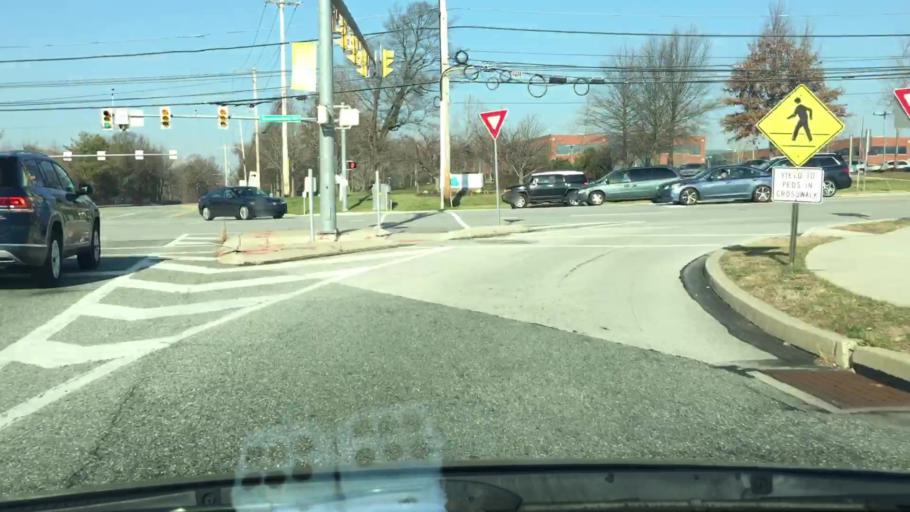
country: US
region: Pennsylvania
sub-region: Montgomery County
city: King of Prussia
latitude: 40.0800
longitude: -75.4127
